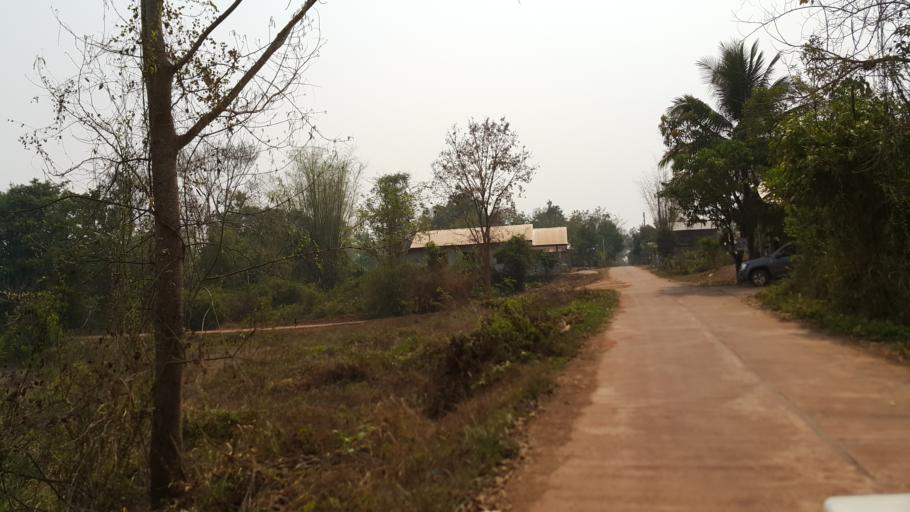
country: TH
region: Nakhon Phanom
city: Ban Phaeng
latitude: 17.8324
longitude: 104.2613
